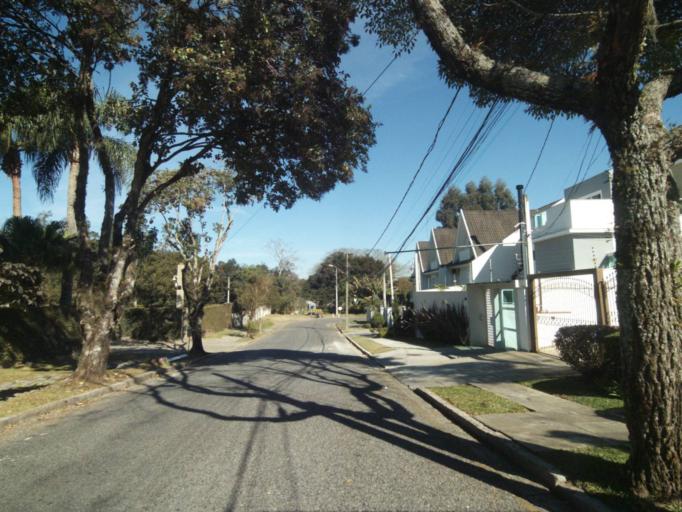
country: BR
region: Parana
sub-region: Curitiba
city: Curitiba
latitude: -25.4128
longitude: -49.2348
